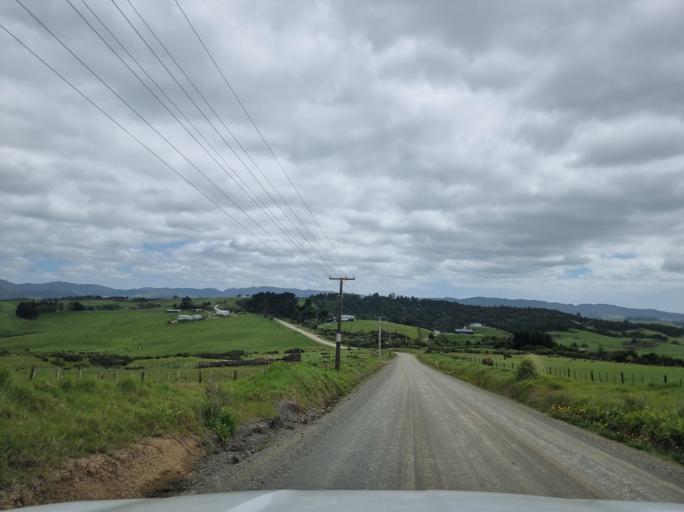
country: NZ
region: Auckland
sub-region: Auckland
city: Wellsford
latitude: -36.1441
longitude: 174.5406
